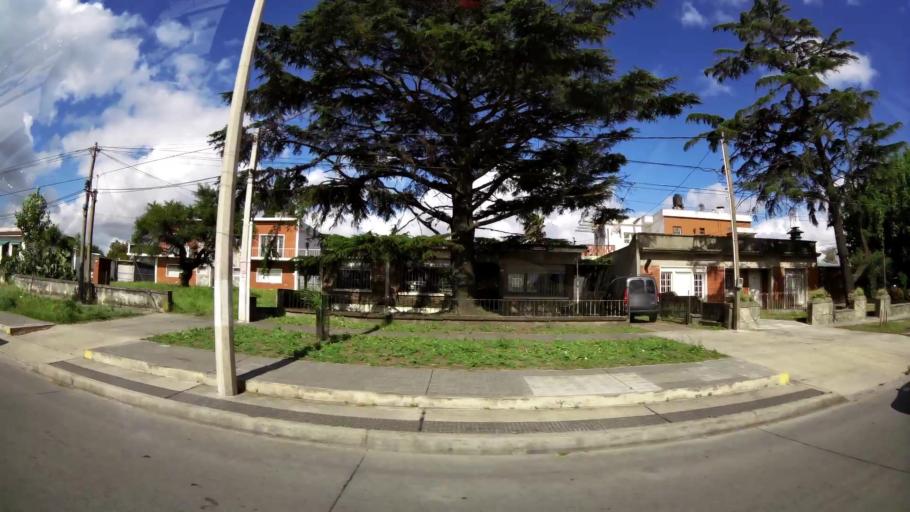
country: UY
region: Canelones
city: La Paz
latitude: -34.8257
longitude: -56.2197
